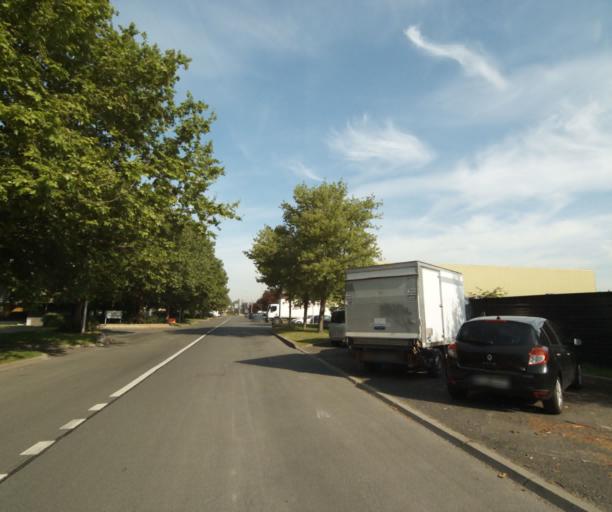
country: FR
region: Ile-de-France
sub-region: Departement des Hauts-de-Seine
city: Bois-Colombes
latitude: 48.9421
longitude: 2.2761
